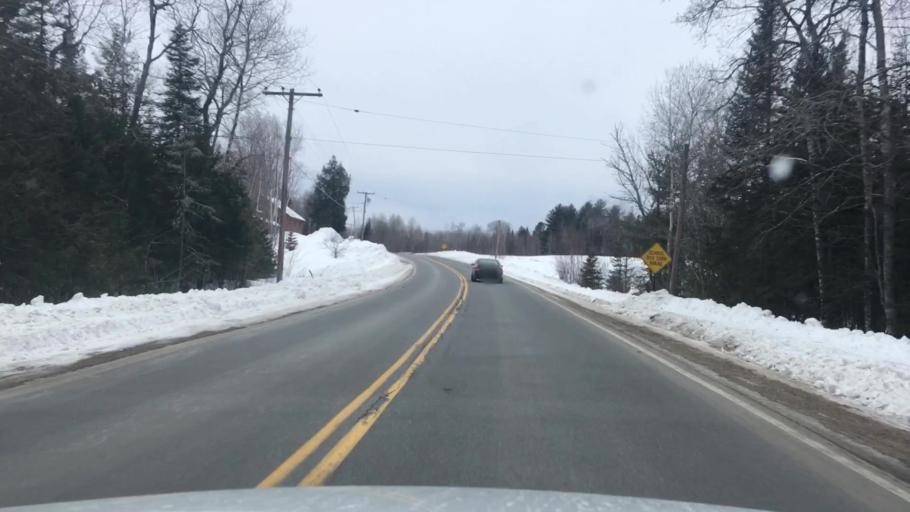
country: US
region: Maine
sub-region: Penobscot County
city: Garland
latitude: 44.9935
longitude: -69.0809
